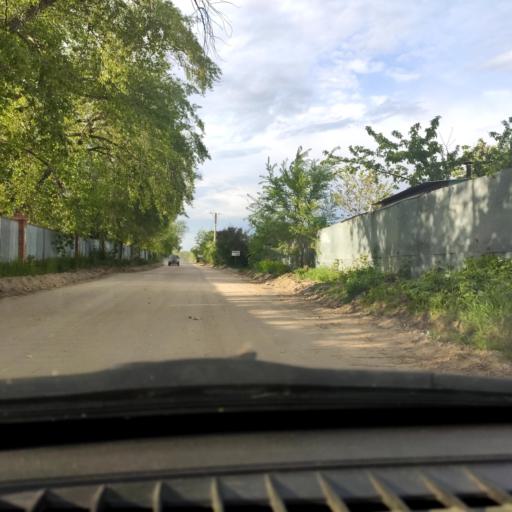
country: RU
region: Samara
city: Zhigulevsk
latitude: 53.4505
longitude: 49.5344
